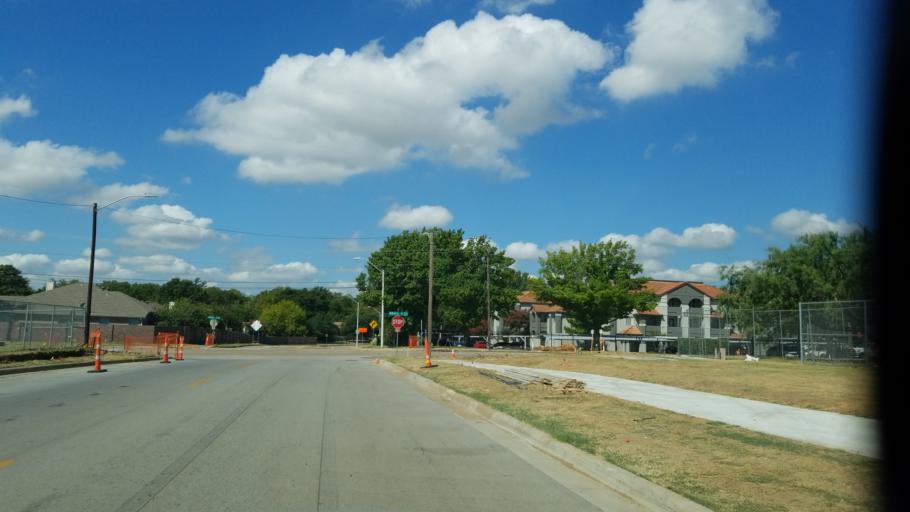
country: US
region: Texas
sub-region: Tarrant County
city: Euless
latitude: 32.8321
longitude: -97.0688
